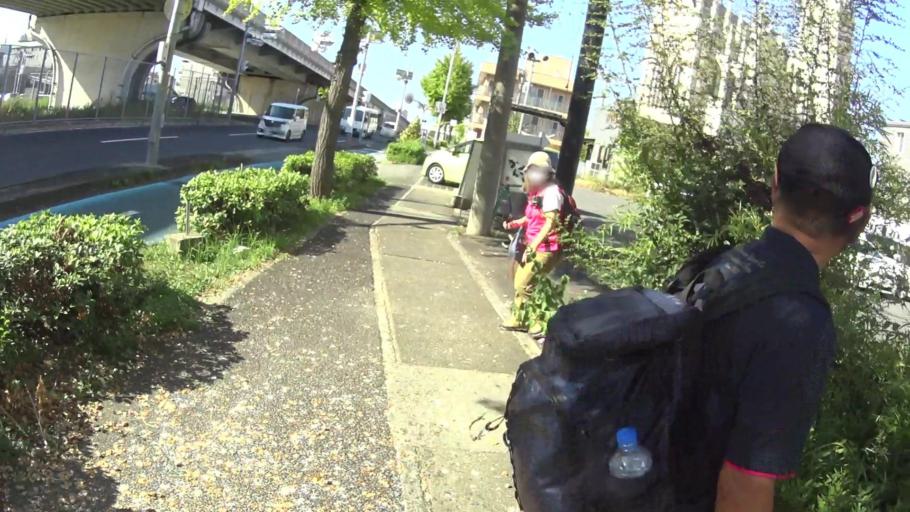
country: JP
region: Ehime
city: Kihoku-cho
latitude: 33.3979
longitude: 132.8615
